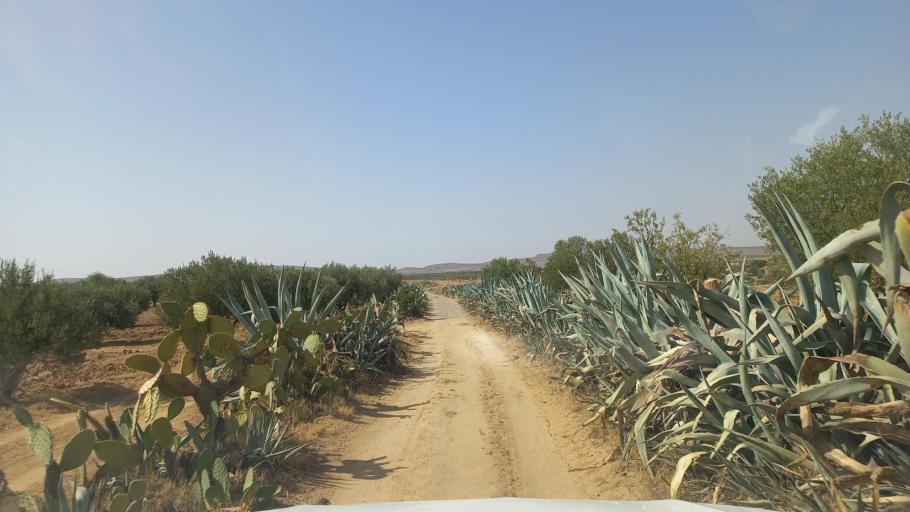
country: TN
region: Al Qasrayn
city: Kasserine
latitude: 35.2303
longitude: 9.0506
